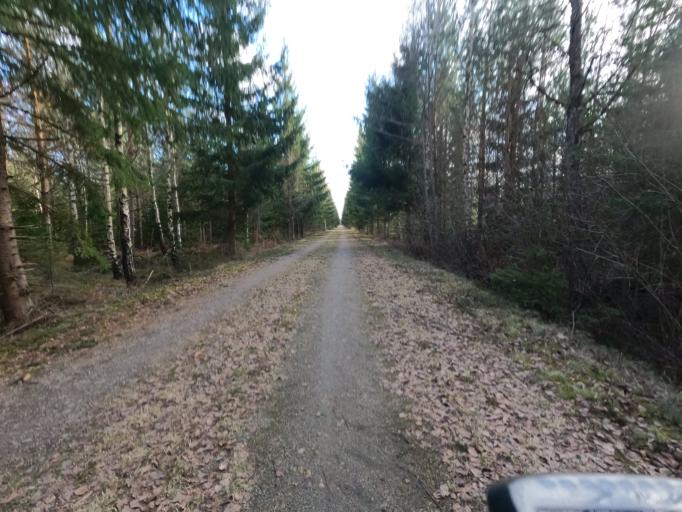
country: SE
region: Kronoberg
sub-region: Alvesta Kommun
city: Vislanda
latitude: 56.6489
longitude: 14.6175
